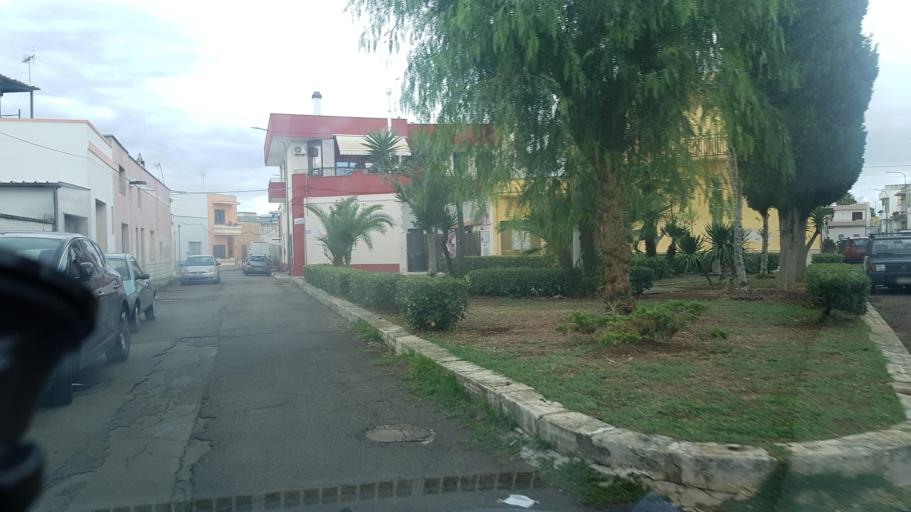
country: IT
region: Apulia
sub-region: Provincia di Lecce
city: Salice Salentino
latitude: 40.3824
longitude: 17.9671
